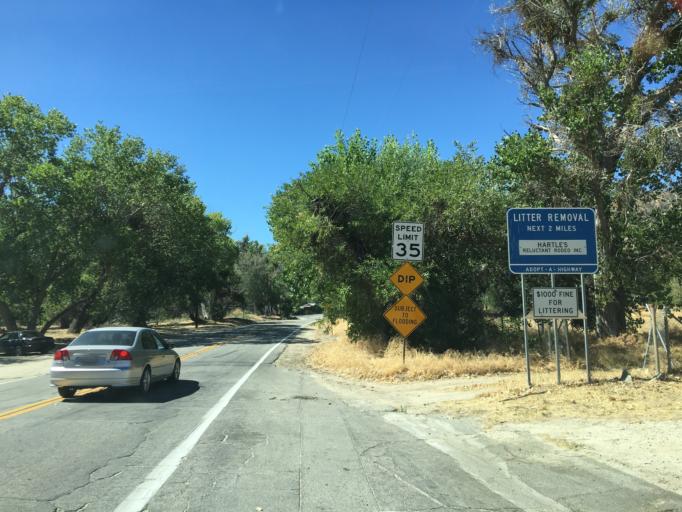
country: US
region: California
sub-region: Los Angeles County
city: Green Valley
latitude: 34.6786
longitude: -118.4523
